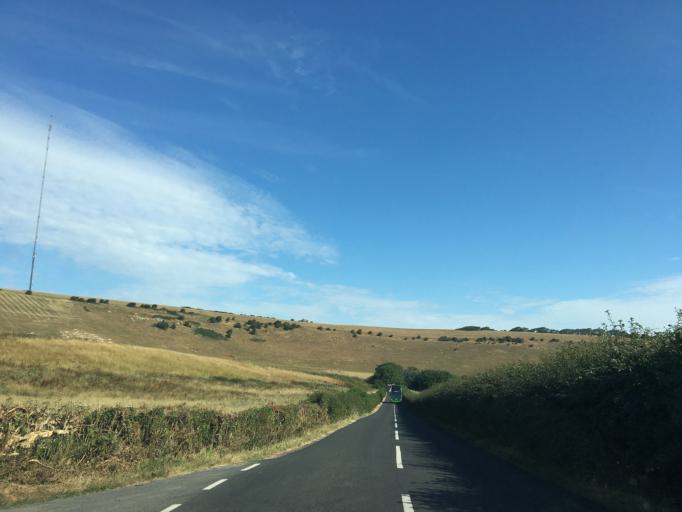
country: GB
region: England
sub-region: Isle of Wight
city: Chale
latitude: 50.6443
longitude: -1.3206
